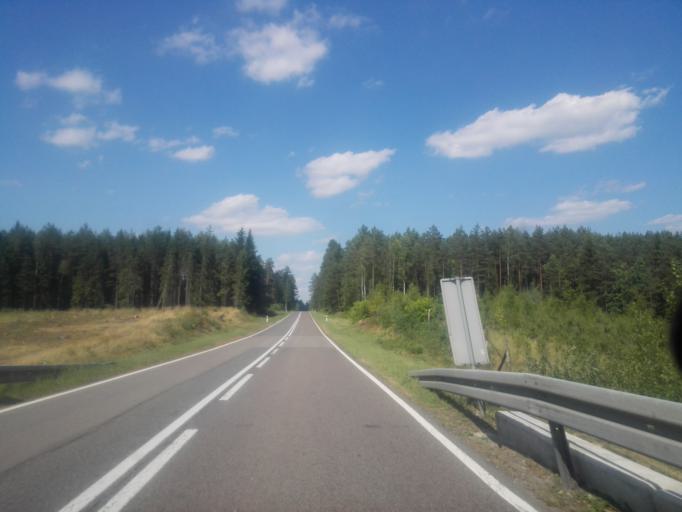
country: PL
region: Podlasie
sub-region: Powiat sejnenski
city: Sejny
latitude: 53.9995
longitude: 23.3143
